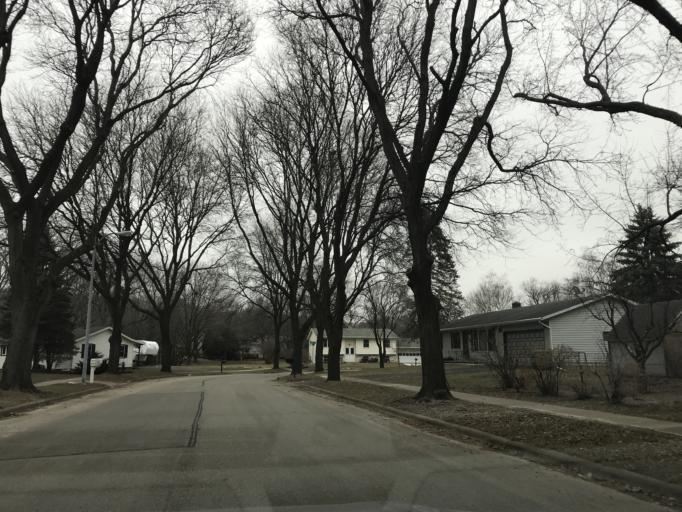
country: US
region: Wisconsin
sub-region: Dane County
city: Monona
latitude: 43.1009
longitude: -89.3047
